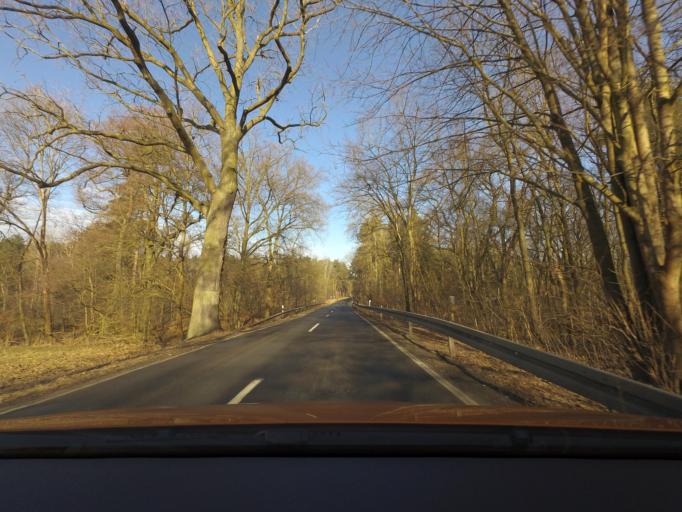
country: DE
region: Brandenburg
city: Wandlitz
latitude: 52.7321
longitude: 13.3682
